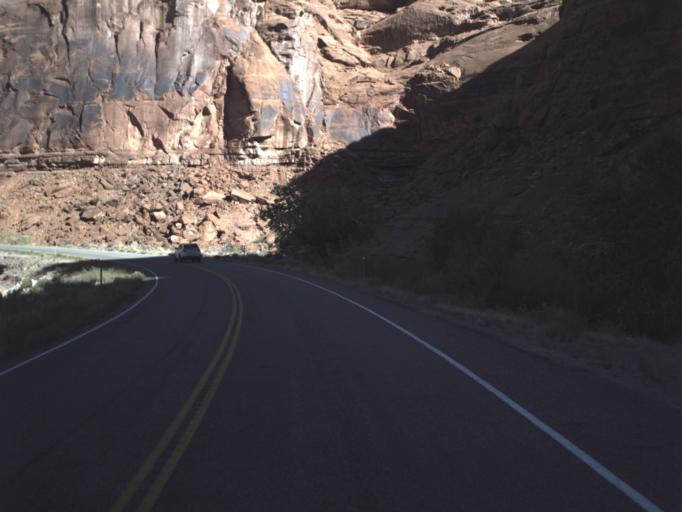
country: US
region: Utah
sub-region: San Juan County
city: Blanding
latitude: 37.9578
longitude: -110.4805
